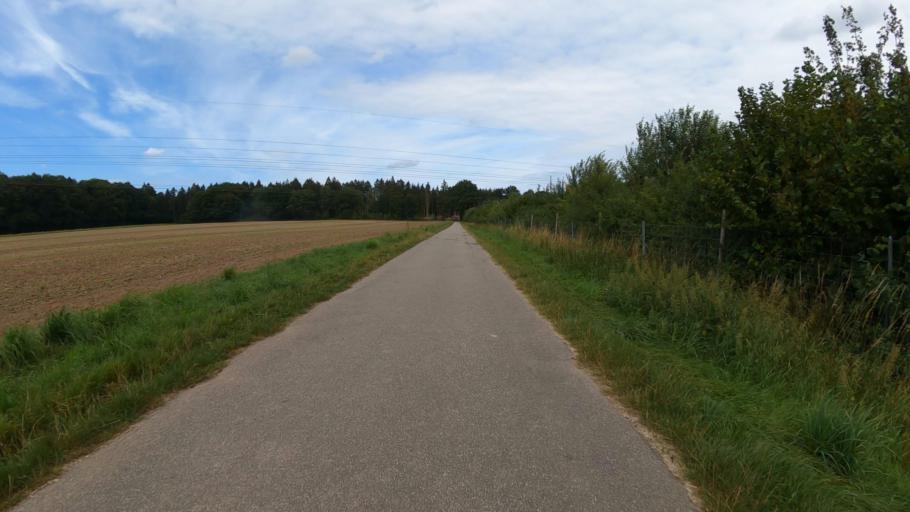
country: DE
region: Lower Saxony
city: Seevetal
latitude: 53.3784
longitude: 9.9274
